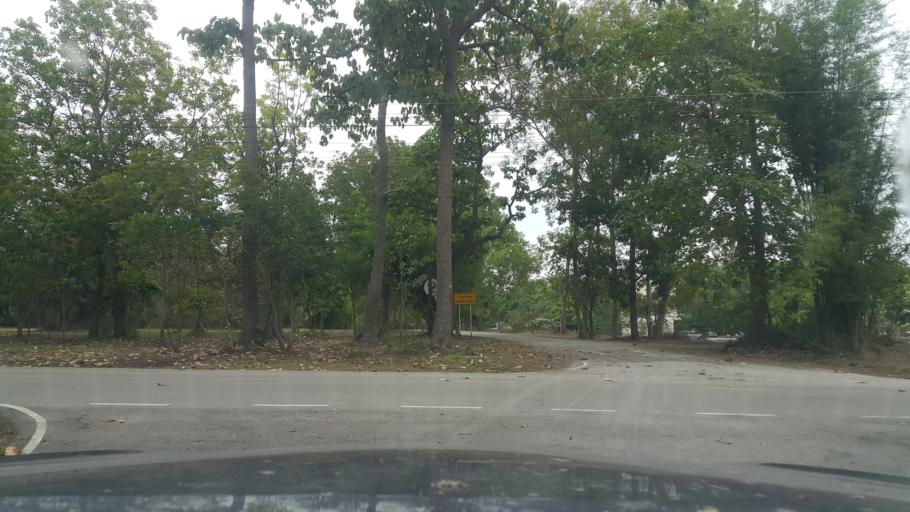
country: TH
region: Chiang Mai
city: San Pa Tong
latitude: 18.6489
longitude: 98.8479
